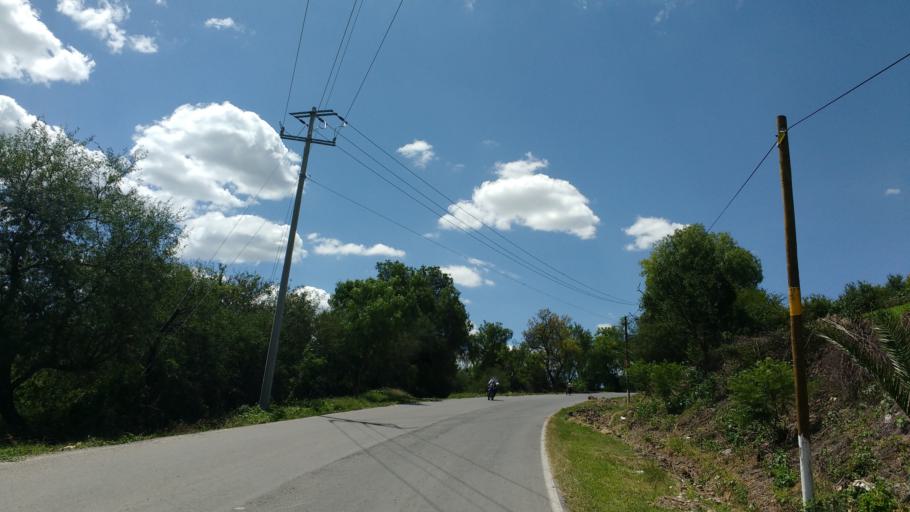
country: MX
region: Hidalgo
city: Mixquiahuala de Juarez
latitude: 20.2423
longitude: -99.2376
